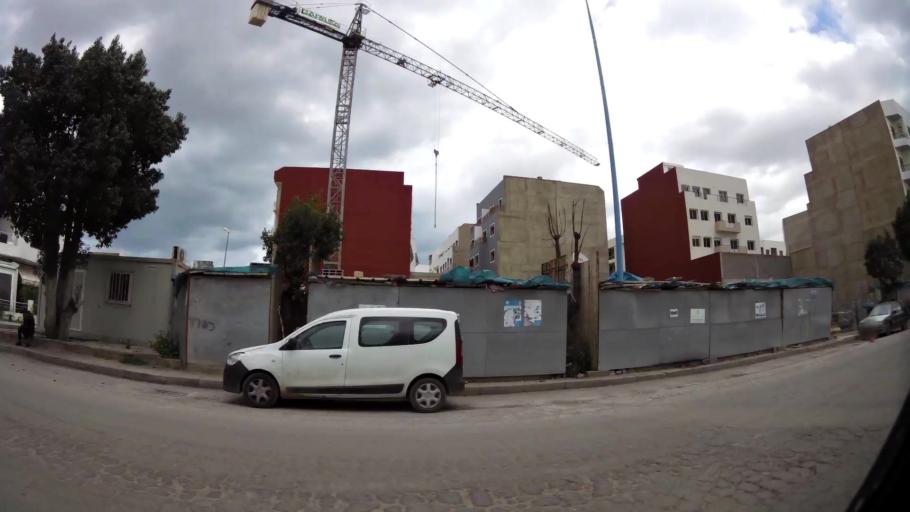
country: MA
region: Grand Casablanca
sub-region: Casablanca
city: Casablanca
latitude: 33.6050
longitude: -7.5485
